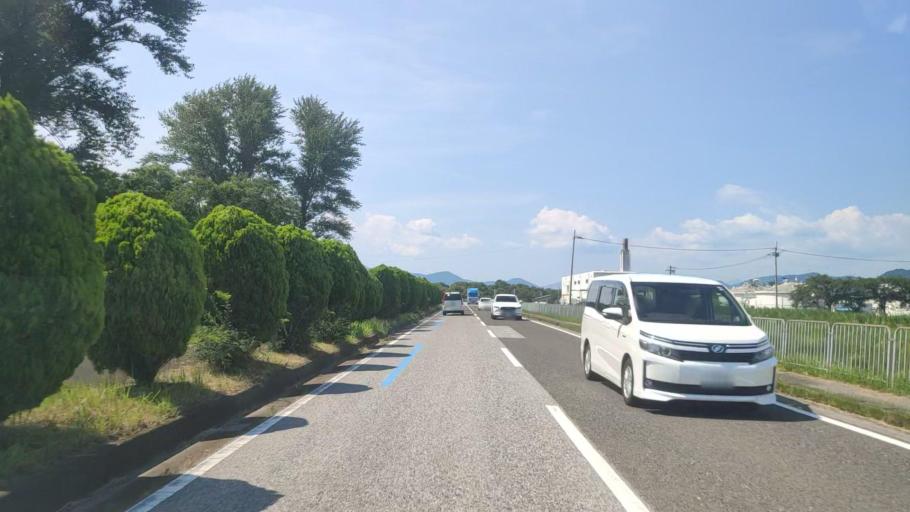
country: JP
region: Shiga Prefecture
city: Nagahama
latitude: 35.4240
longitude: 136.1976
